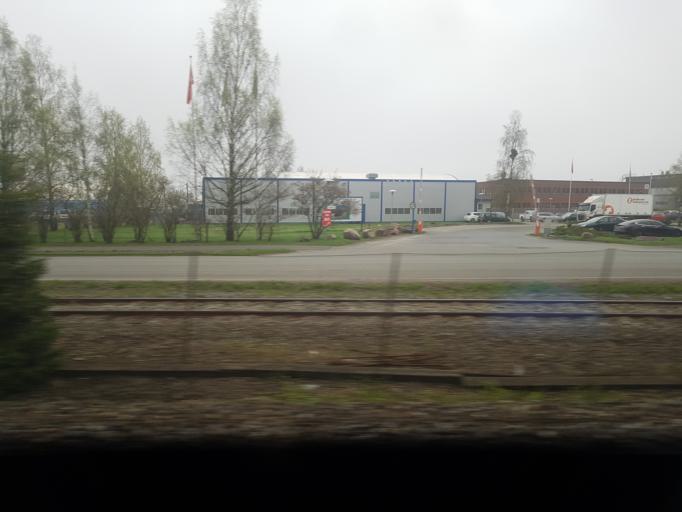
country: NO
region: Buskerud
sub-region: Drammen
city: Skoger
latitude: 59.7493
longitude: 10.2496
